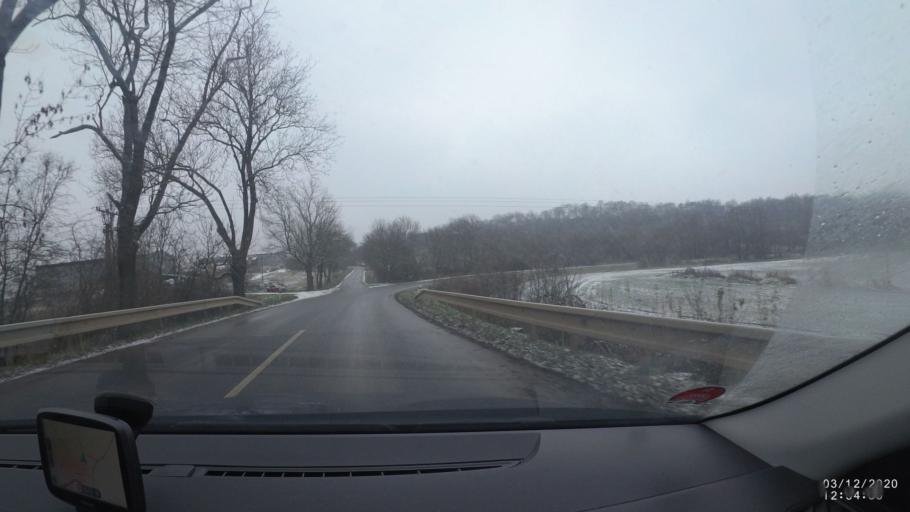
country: CZ
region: Central Bohemia
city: Revnicov
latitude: 50.1896
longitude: 13.8124
